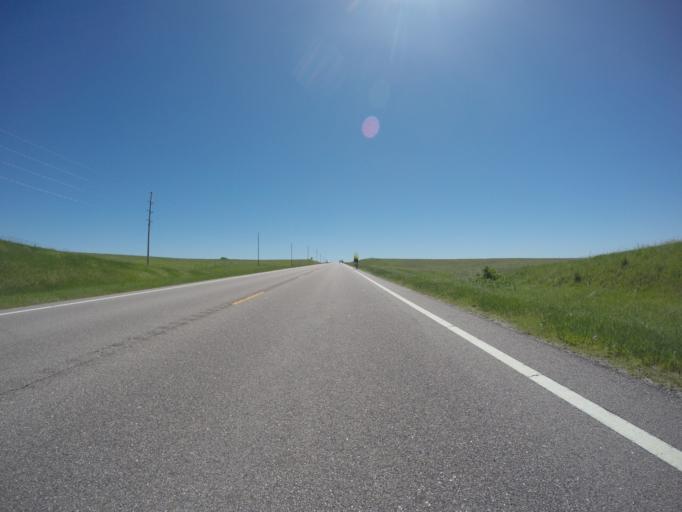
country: US
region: Kansas
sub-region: Norton County
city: Norton
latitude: 39.8283
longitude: -99.6929
